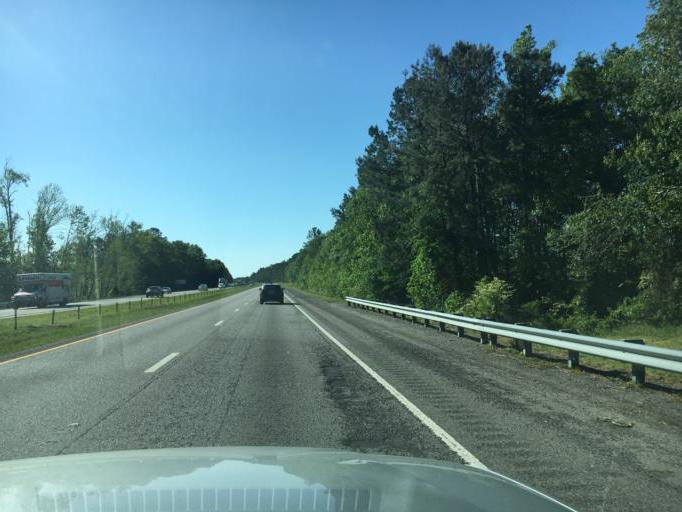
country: US
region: South Carolina
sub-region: Orangeburg County
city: Brookdale
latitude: 33.5313
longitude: -80.8017
